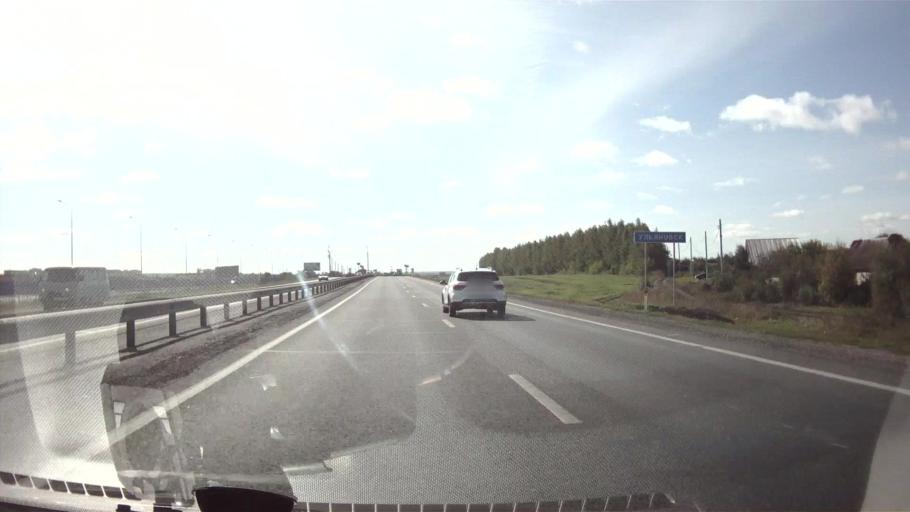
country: RU
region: Ulyanovsk
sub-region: Ulyanovskiy Rayon
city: Ulyanovsk
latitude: 54.2805
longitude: 48.2595
